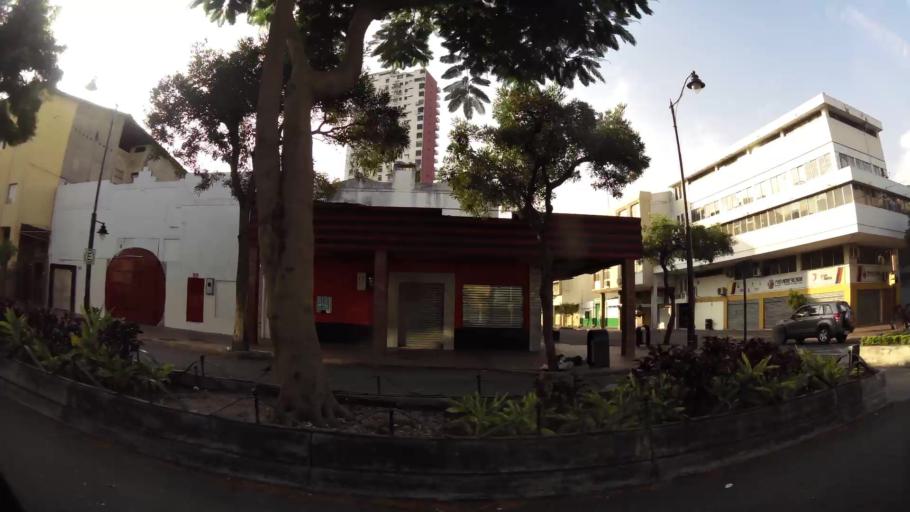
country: EC
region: Guayas
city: Eloy Alfaro
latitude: -2.1862
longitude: -79.8789
